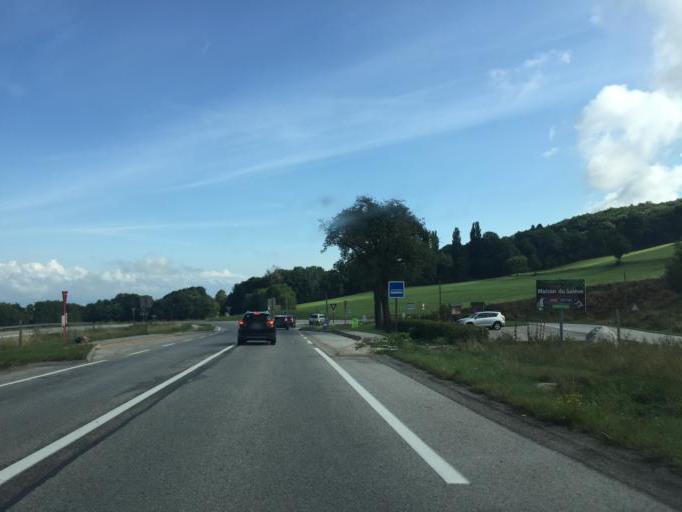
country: FR
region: Rhone-Alpes
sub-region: Departement de la Haute-Savoie
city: Beaumont
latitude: 46.0843
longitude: 6.1009
